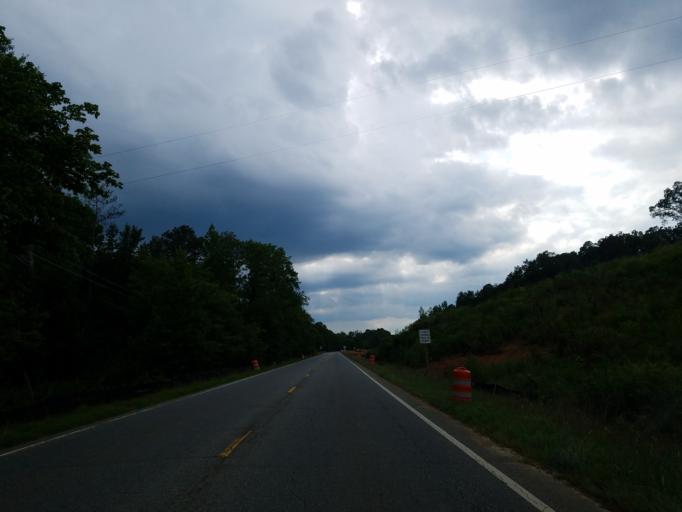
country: US
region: Georgia
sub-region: Floyd County
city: Shannon
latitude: 34.3688
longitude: -85.0101
